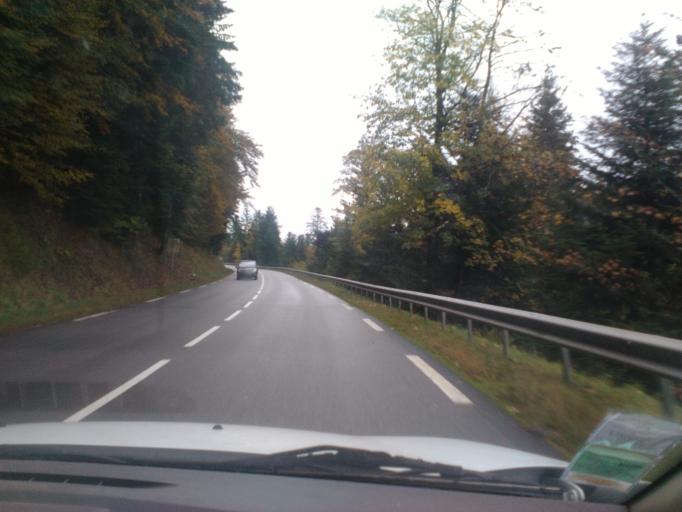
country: FR
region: Lorraine
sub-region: Departement des Vosges
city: Xonrupt-Longemer
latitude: 48.1107
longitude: 6.9095
